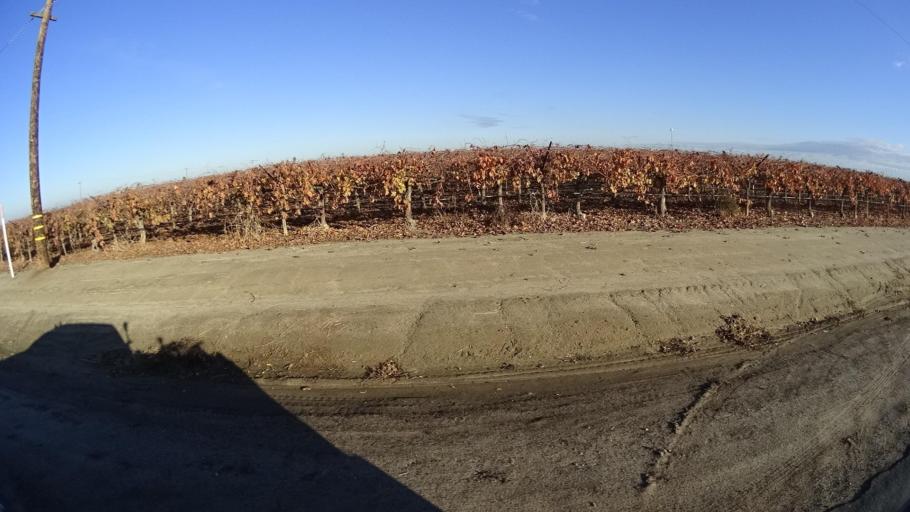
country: US
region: California
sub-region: Kern County
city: Delano
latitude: 35.7904
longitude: -119.2843
